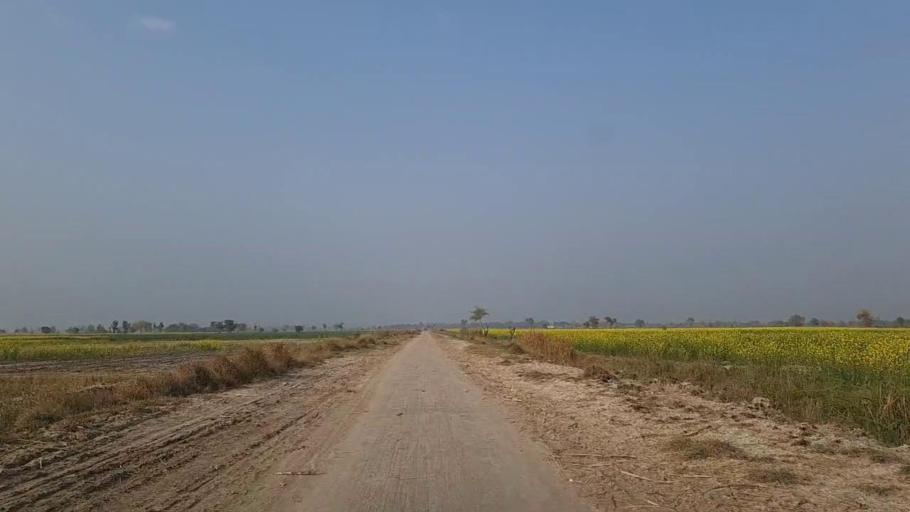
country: PK
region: Sindh
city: Jam Sahib
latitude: 26.3363
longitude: 68.5148
